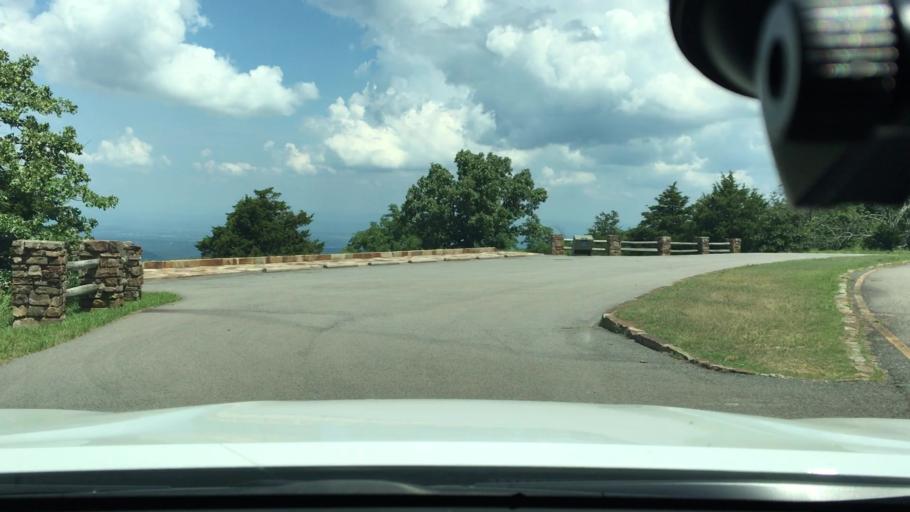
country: US
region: Arkansas
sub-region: Logan County
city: Paris
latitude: 35.1722
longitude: -93.6475
